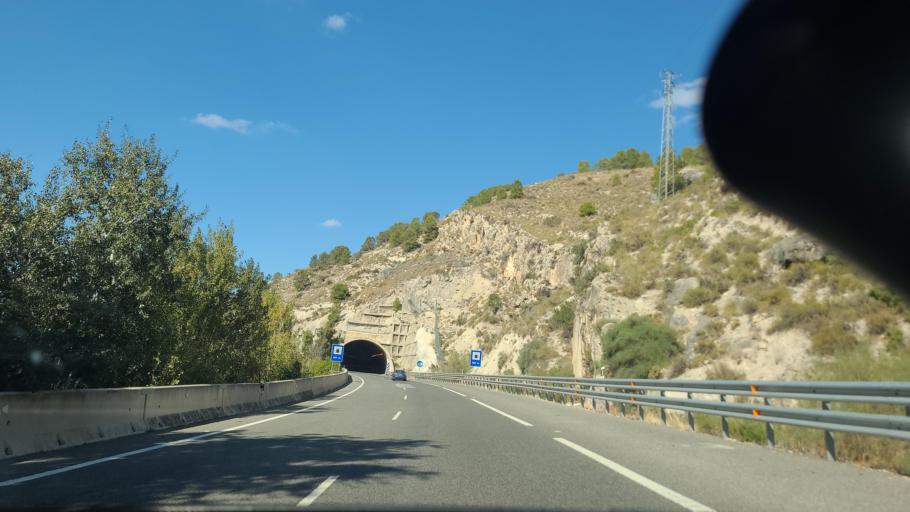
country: ES
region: Andalusia
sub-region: Provincia de Jaen
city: Pegalajar
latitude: 37.6883
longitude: -3.6296
